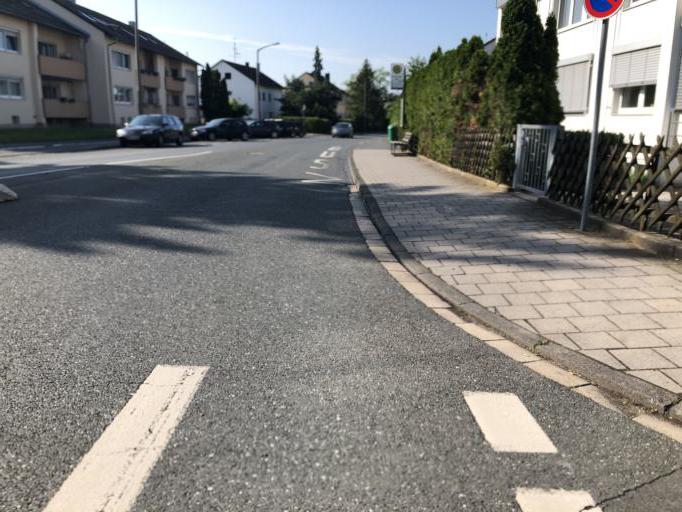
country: DE
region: Bavaria
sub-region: Regierungsbezirk Mittelfranken
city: Erlangen
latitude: 49.5760
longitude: 10.9930
